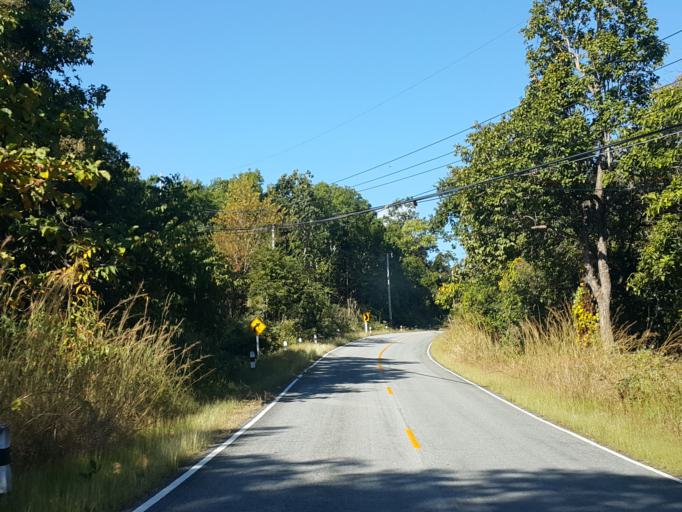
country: TH
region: Chiang Mai
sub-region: Amphoe Chiang Dao
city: Chiang Dao
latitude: 19.5116
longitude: 98.9166
